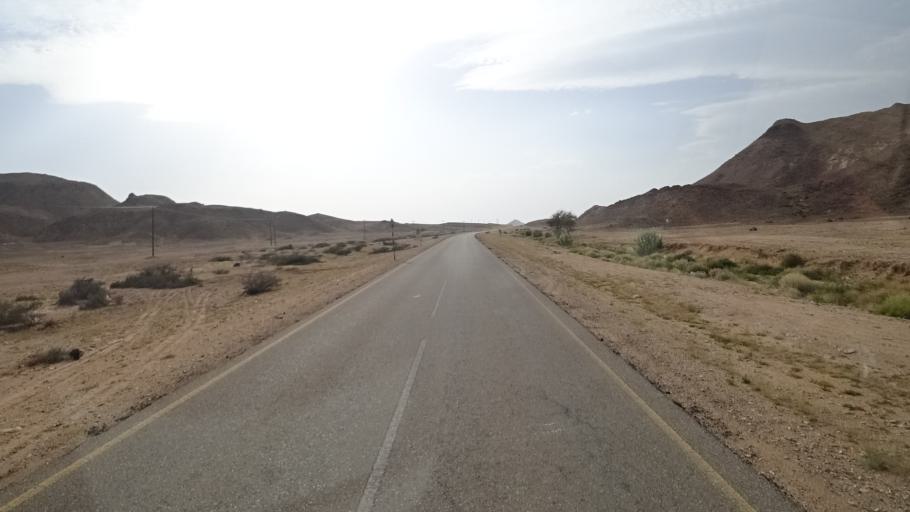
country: OM
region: Ash Sharqiyah
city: Sur
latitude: 22.4344
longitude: 59.8116
